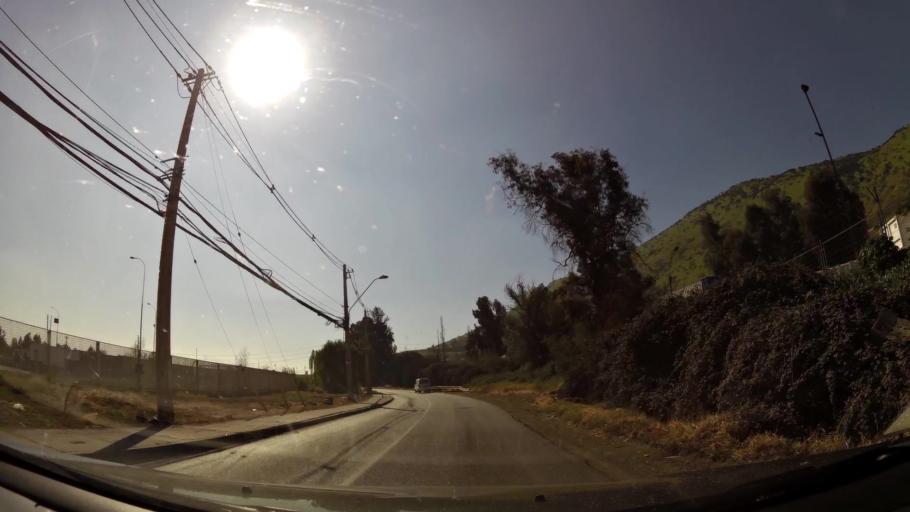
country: CL
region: Santiago Metropolitan
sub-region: Provincia de Chacabuco
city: Chicureo Abajo
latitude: -33.3310
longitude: -70.6985
